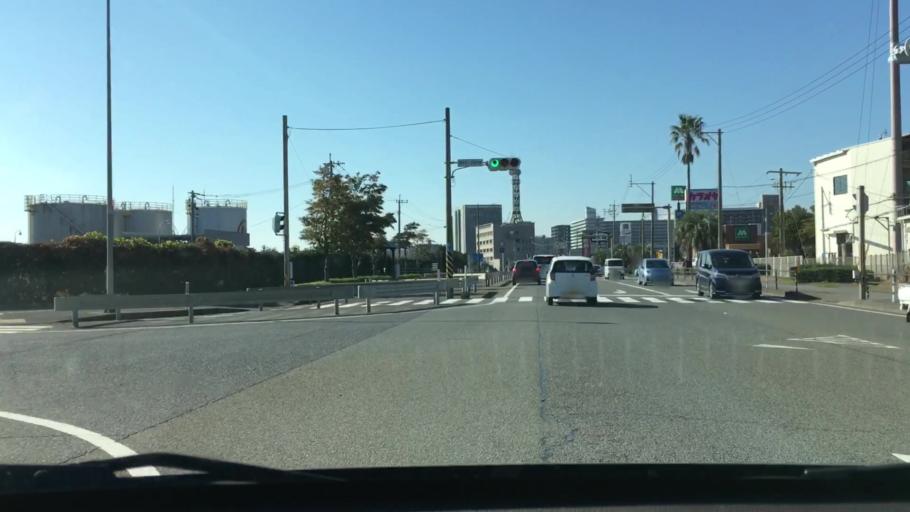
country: JP
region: Kagoshima
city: Kagoshima-shi
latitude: 31.6029
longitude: 130.5673
